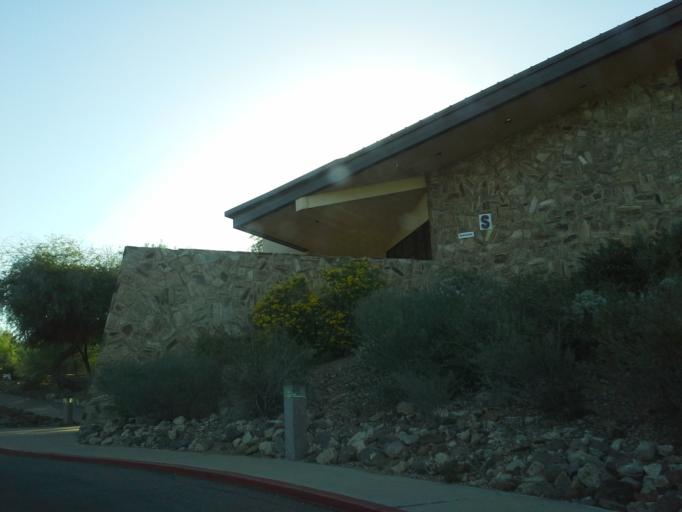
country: US
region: Arizona
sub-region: Maricopa County
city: Glendale
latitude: 33.6029
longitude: -112.0839
